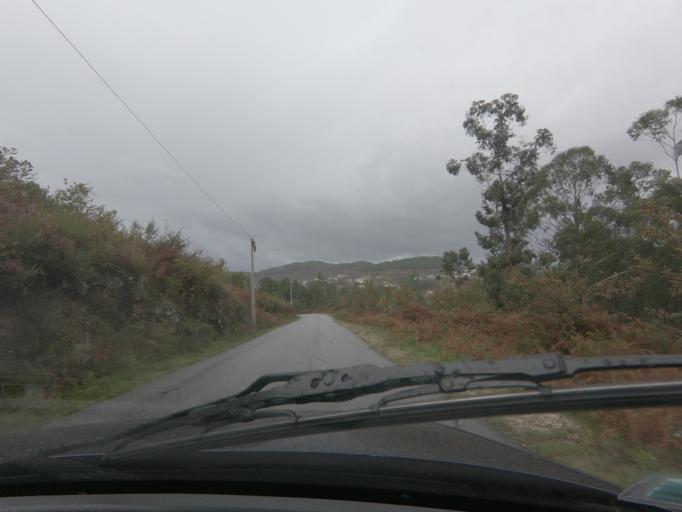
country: PT
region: Vila Real
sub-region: Mondim de Basto
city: Mondim de Basto
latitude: 41.3728
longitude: -7.9435
